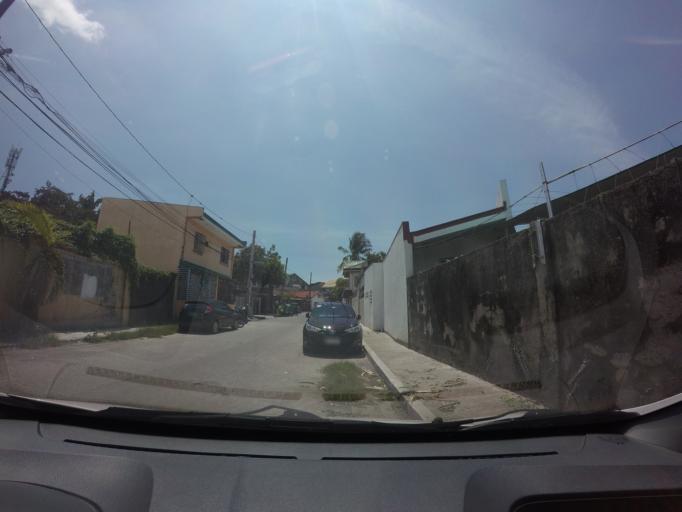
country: PH
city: Sambayanihan People's Village
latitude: 14.4251
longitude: 121.0138
